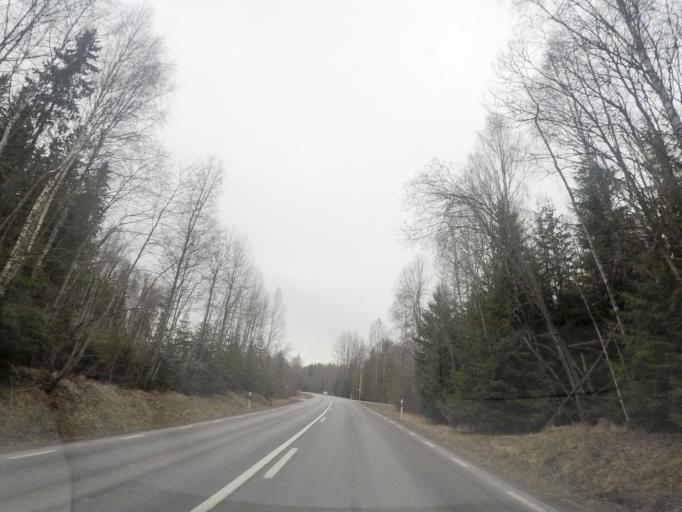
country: SE
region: Vaestmanland
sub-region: Skinnskattebergs Kommun
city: Skinnskatteberg
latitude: 59.8445
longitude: 15.6786
